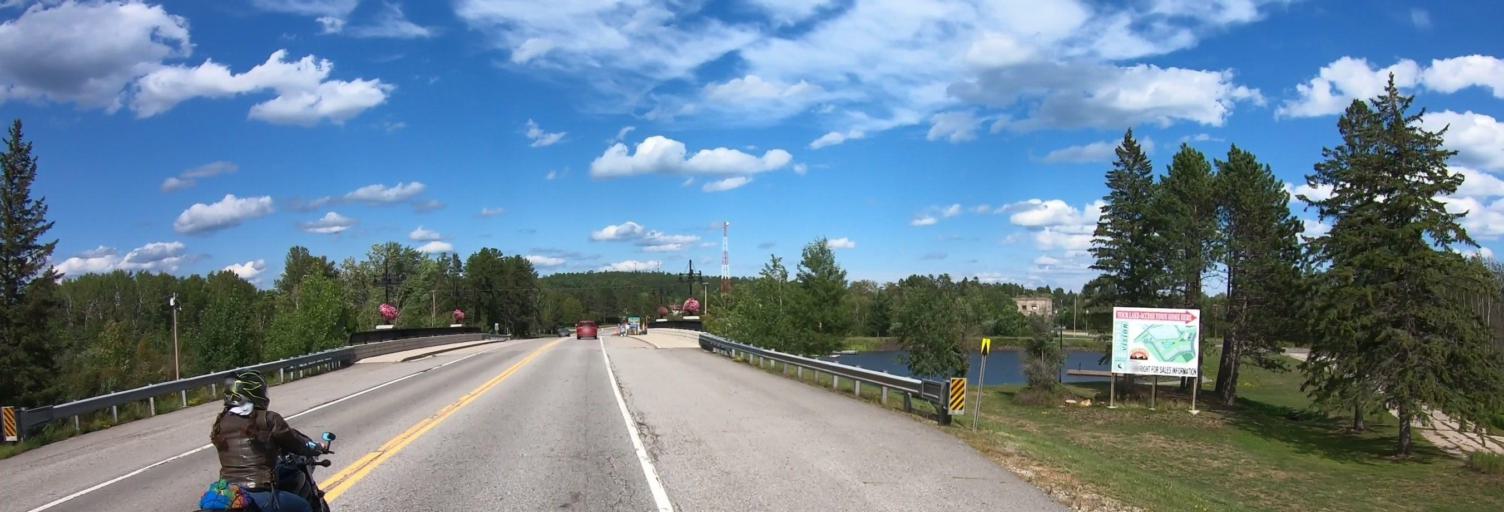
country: US
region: Minnesota
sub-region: Saint Louis County
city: Aurora
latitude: 47.8034
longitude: -92.2828
